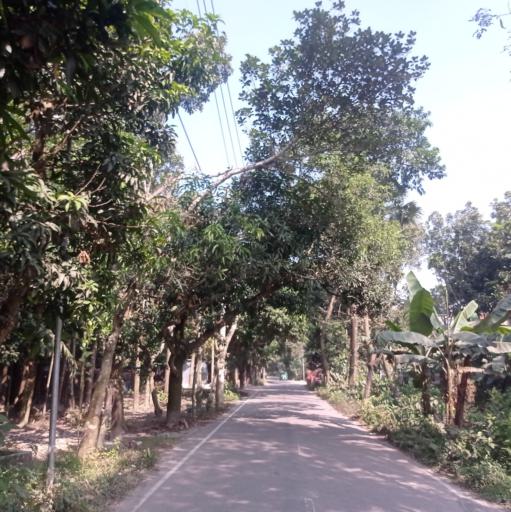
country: BD
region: Dhaka
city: Narsingdi
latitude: 24.0275
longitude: 90.6714
